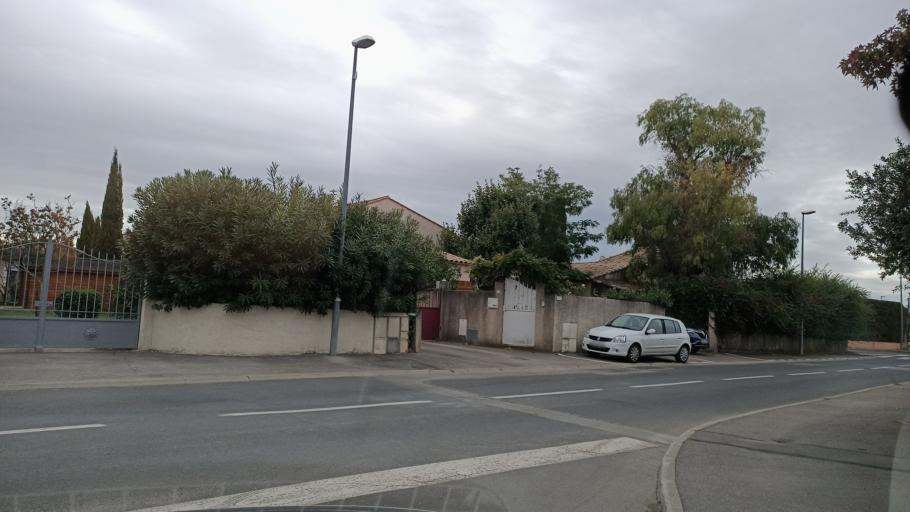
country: FR
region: Languedoc-Roussillon
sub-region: Departement de l'Herault
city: Lunel
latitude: 43.6850
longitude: 4.1405
